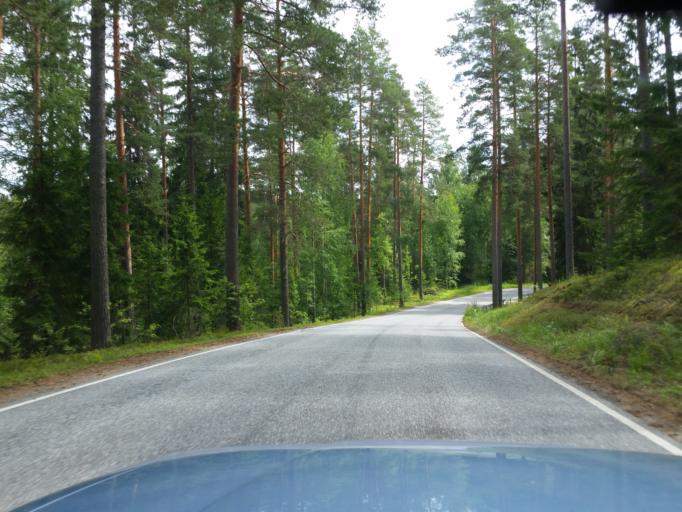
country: FI
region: Southern Savonia
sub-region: Savonlinna
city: Sulkava
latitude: 61.7929
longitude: 28.4210
